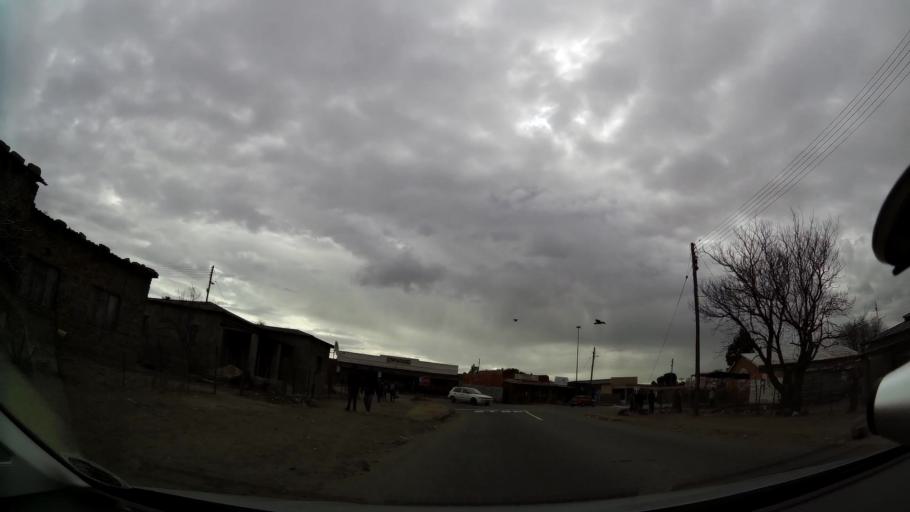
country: ZA
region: Orange Free State
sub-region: Fezile Dabi District Municipality
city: Kroonstad
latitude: -27.6517
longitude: 27.2082
